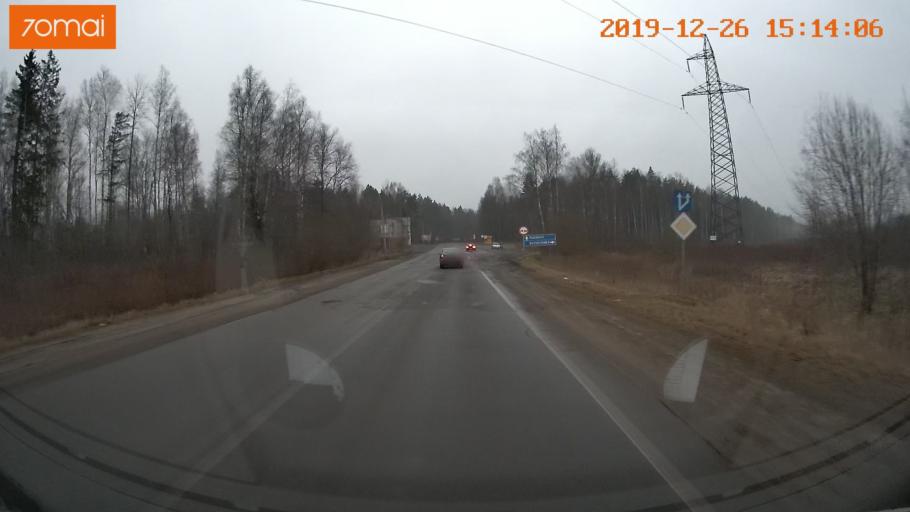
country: RU
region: Jaroslavl
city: Rybinsk
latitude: 58.1091
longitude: 38.8818
